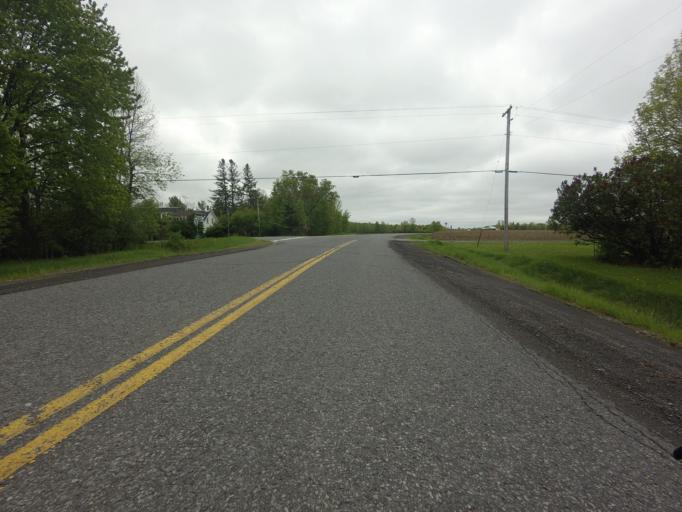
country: US
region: New York
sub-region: St. Lawrence County
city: Norfolk
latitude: 44.9827
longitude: -75.1553
